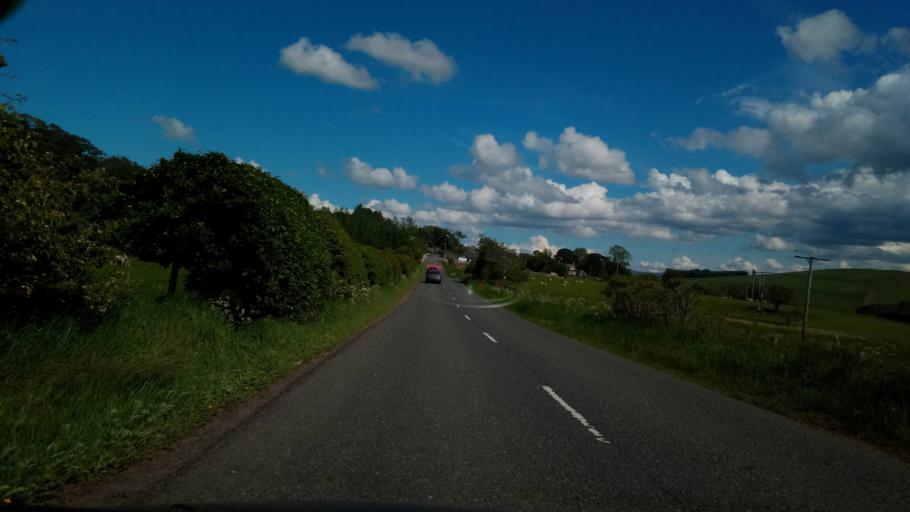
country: GB
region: Scotland
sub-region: The Scottish Borders
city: Jedburgh
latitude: 55.3881
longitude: -2.6014
